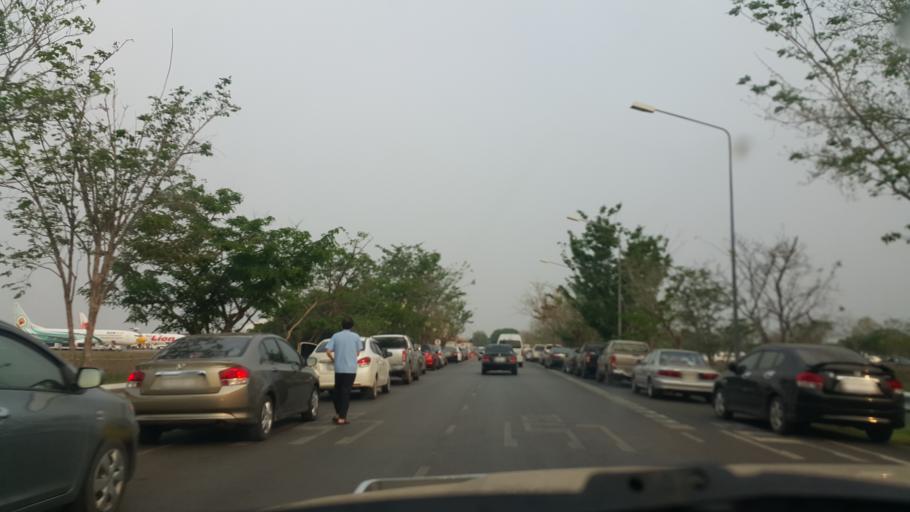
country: TH
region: Changwat Udon Thani
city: Udon Thani
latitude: 17.3877
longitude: 102.7730
